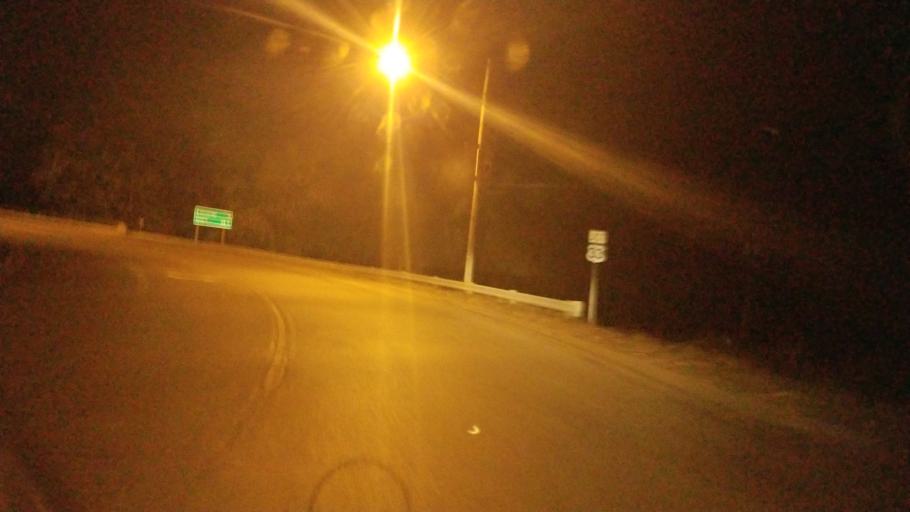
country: US
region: Ohio
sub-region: Hocking County
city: Logan
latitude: 39.5332
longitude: -82.4080
